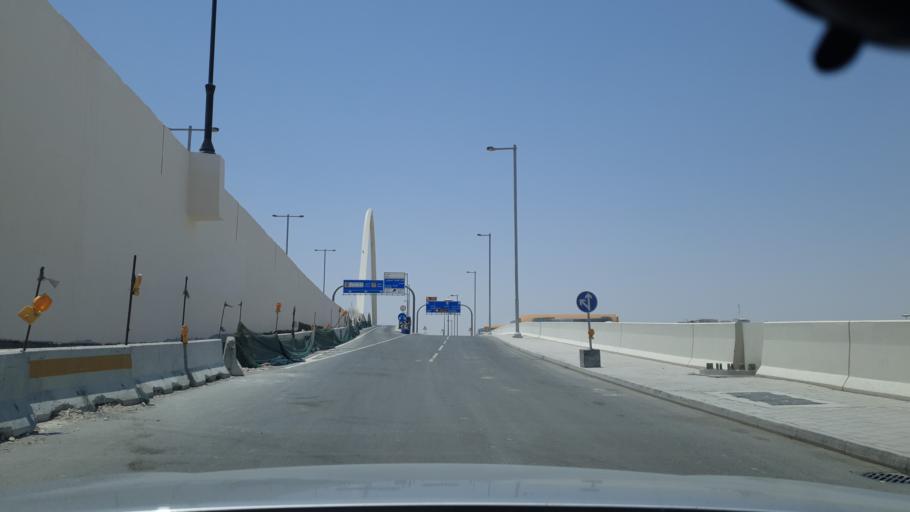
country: QA
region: Baladiyat Umm Salal
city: Umm Salal Muhammad
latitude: 25.4017
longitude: 51.5179
